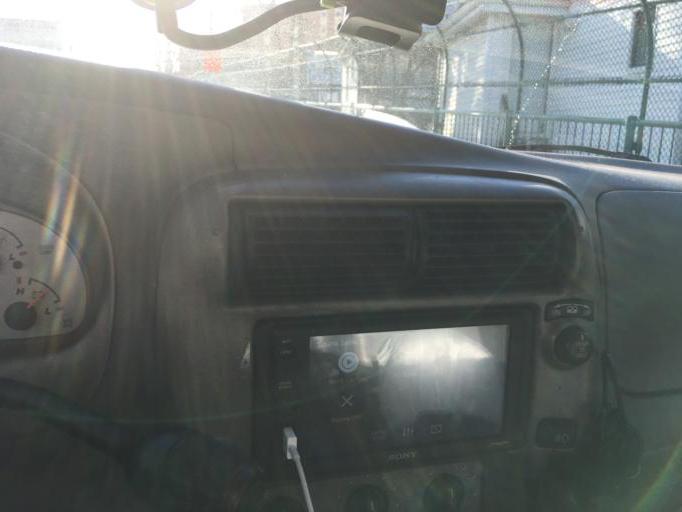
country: US
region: Massachusetts
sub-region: Middlesex County
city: Somerville
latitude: 42.3864
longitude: -71.0909
